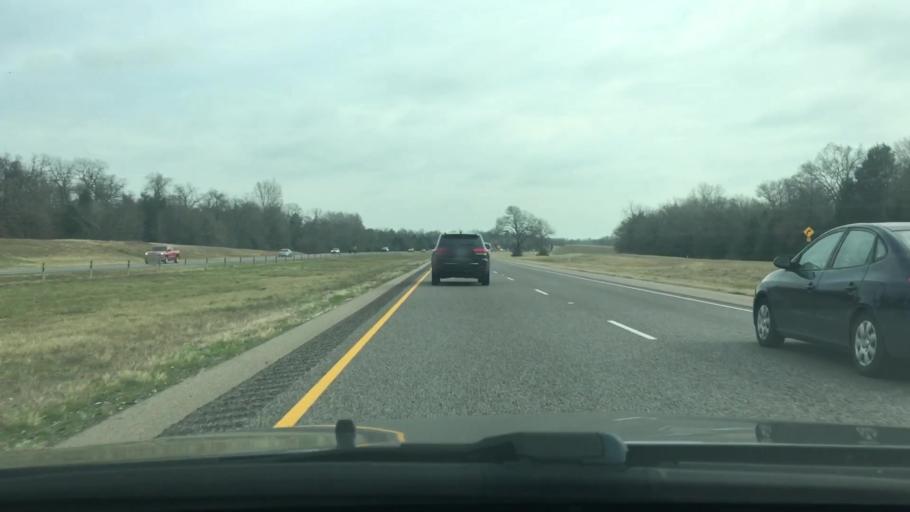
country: US
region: Texas
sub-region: Leon County
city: Buffalo
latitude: 31.5062
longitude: -96.1004
